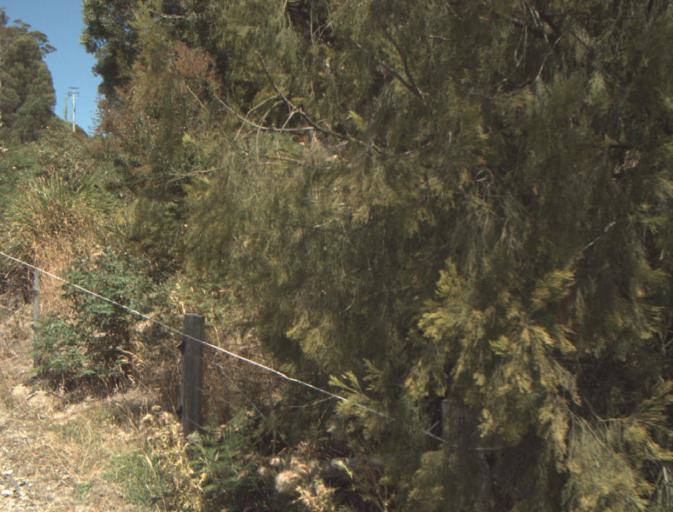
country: AU
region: Tasmania
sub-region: Launceston
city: Mayfield
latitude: -41.2662
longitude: 147.1488
